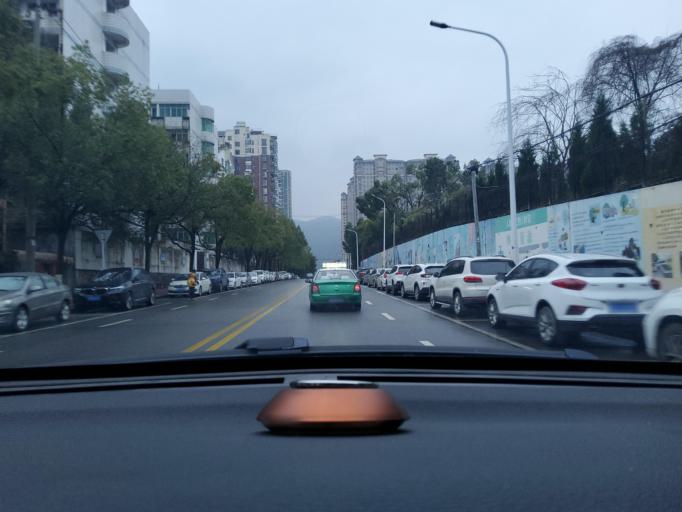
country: CN
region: Hubei
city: Tuanchengshan
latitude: 30.1924
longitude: 115.0275
